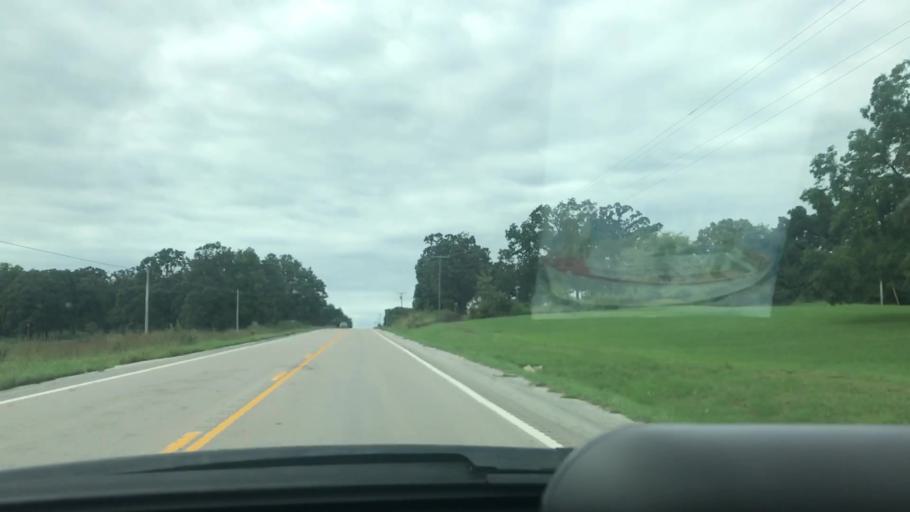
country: US
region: Missouri
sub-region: Benton County
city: Warsaw
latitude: 38.1376
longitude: -93.2842
